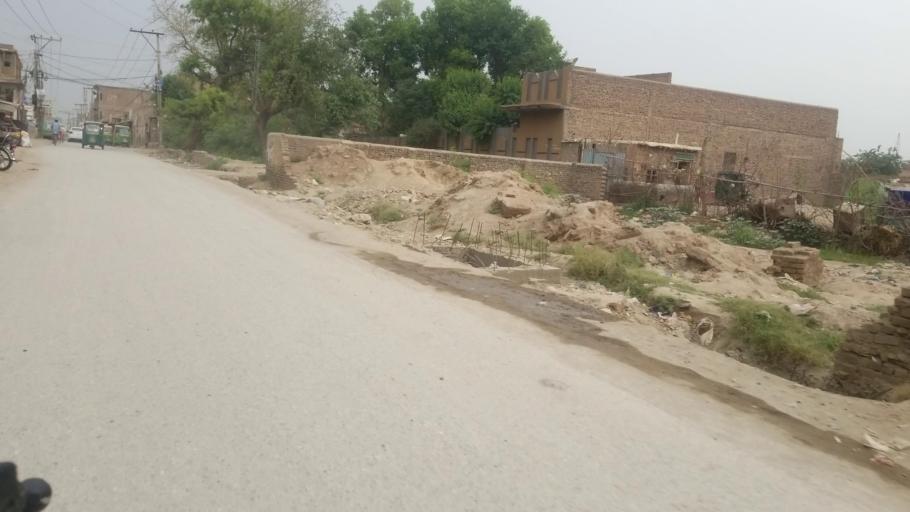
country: PK
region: Khyber Pakhtunkhwa
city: Peshawar
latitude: 33.9884
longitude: 71.5508
